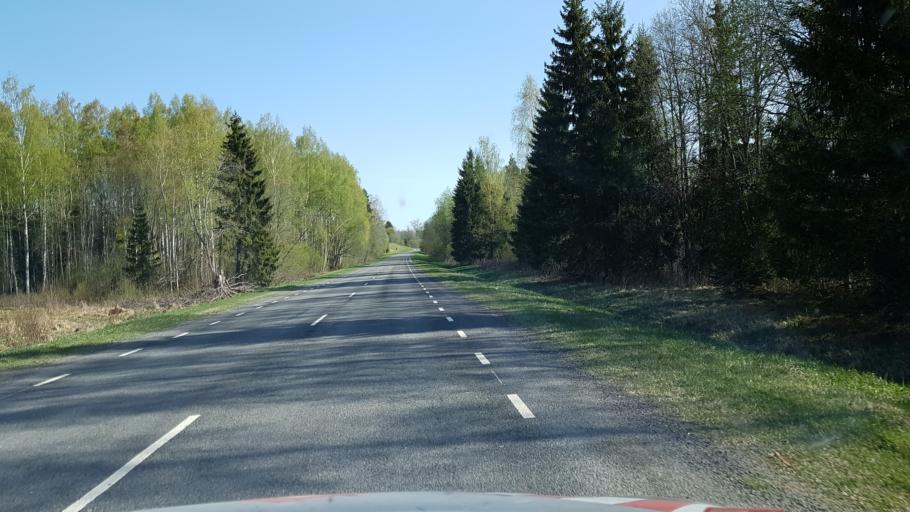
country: EE
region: Viljandimaa
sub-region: Karksi vald
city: Karksi-Nuia
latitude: 58.2312
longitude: 25.5797
